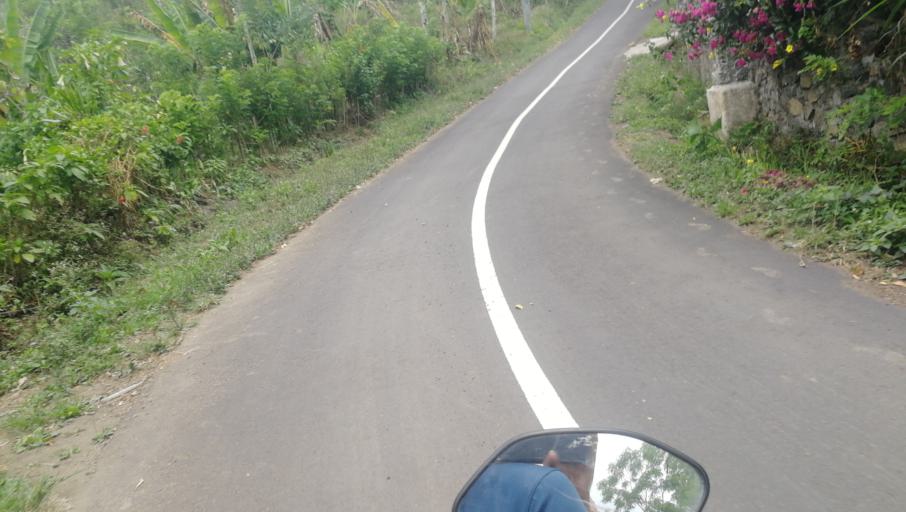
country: ID
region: Bali
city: Munduk
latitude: -8.3051
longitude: 115.0607
